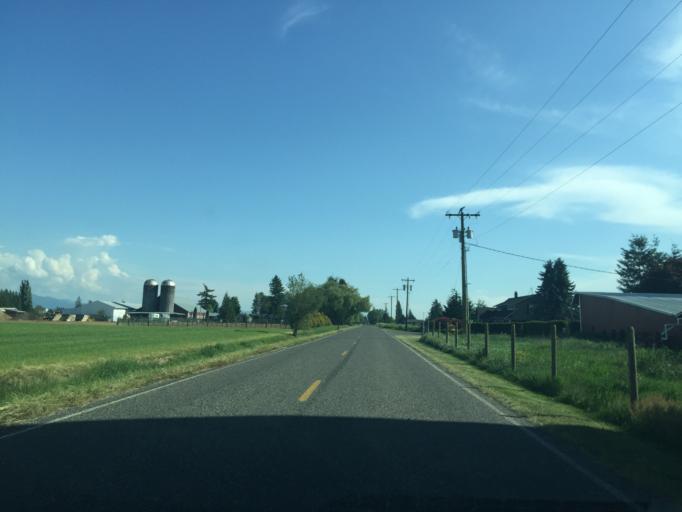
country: US
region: Washington
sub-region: Whatcom County
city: Lynden
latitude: 48.9693
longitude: -122.4630
